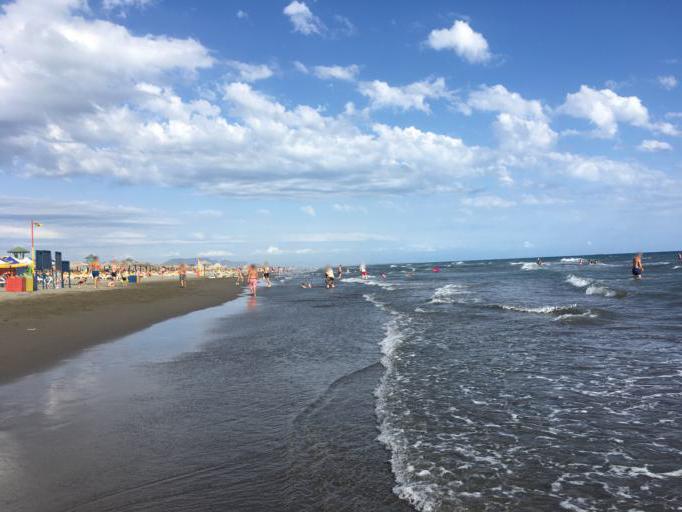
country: ME
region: Ulcinj
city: Ulcinj
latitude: 41.9071
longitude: 19.2484
